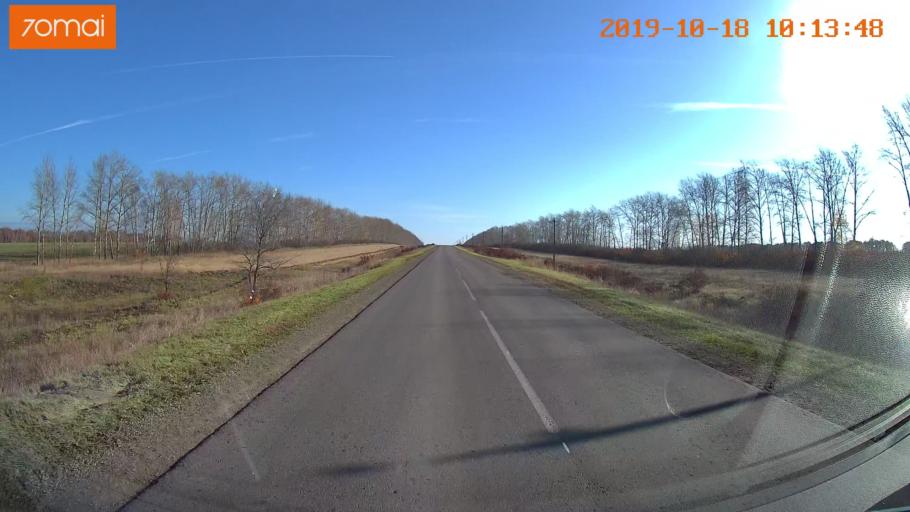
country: RU
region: Tula
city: Kurkino
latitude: 53.4030
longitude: 38.5268
